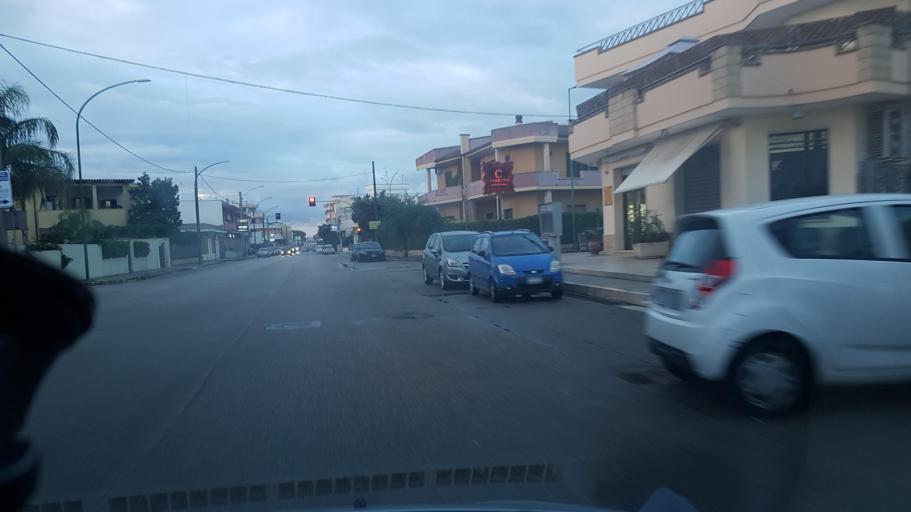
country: IT
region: Apulia
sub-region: Provincia di Lecce
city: Surbo
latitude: 40.3872
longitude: 18.1337
